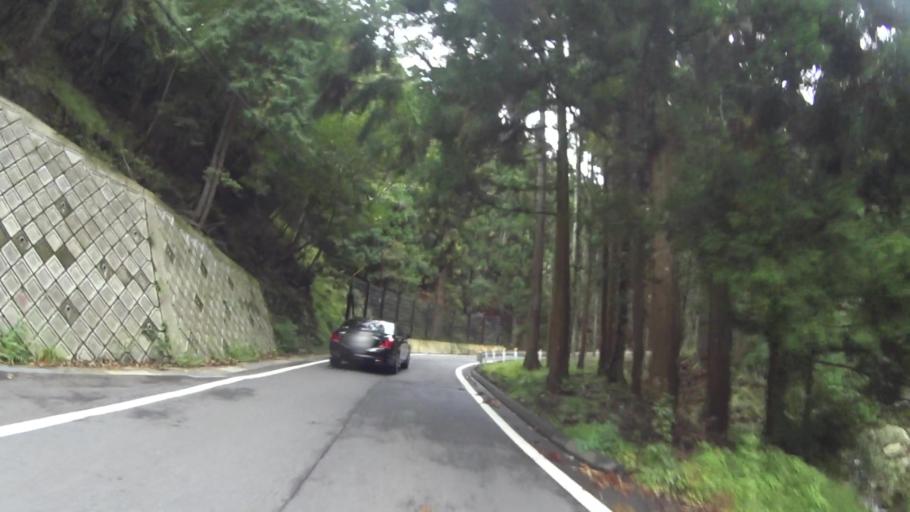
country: JP
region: Kyoto
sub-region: Kyoto-shi
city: Kamigyo-ku
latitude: 35.1413
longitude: 135.7808
